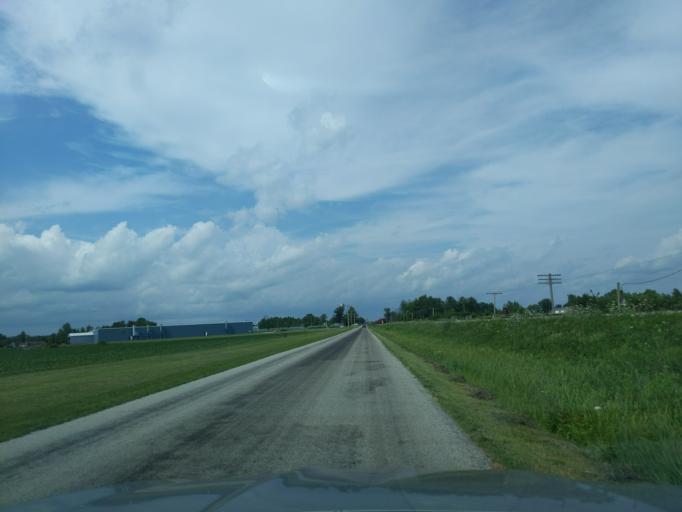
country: US
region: Indiana
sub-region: Ripley County
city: Osgood
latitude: 39.1204
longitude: -85.3016
